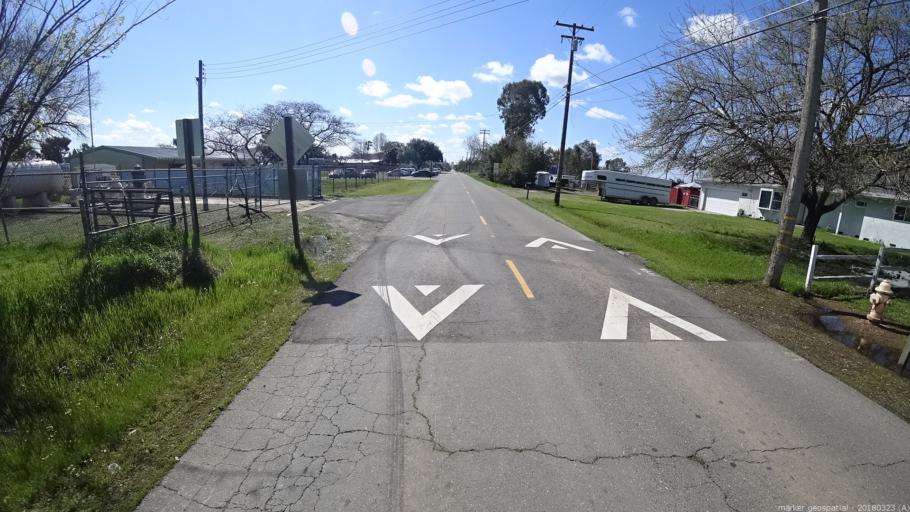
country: US
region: California
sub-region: Sacramento County
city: Rio Linda
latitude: 38.6853
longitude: -121.4199
